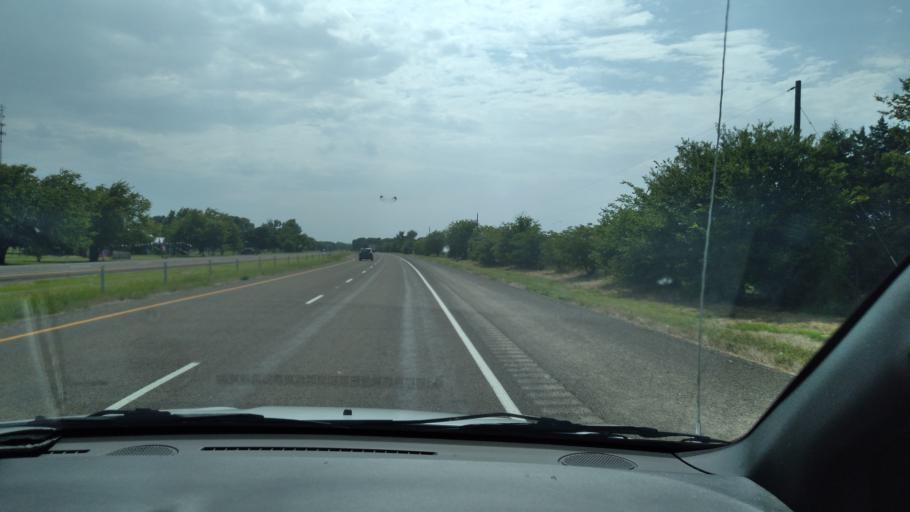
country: US
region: Texas
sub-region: Navarro County
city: Kerens
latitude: 32.1293
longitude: -96.2573
